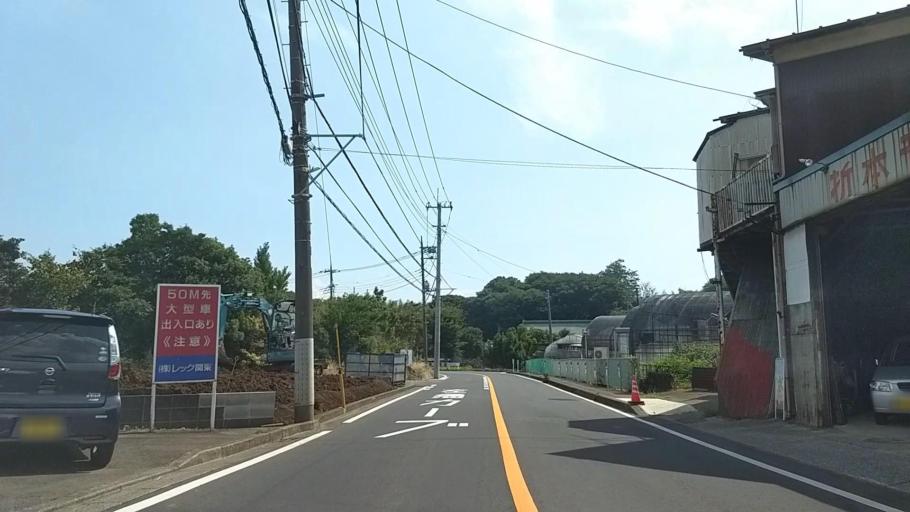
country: JP
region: Kanagawa
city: Yokohama
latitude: 35.5281
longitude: 139.5885
